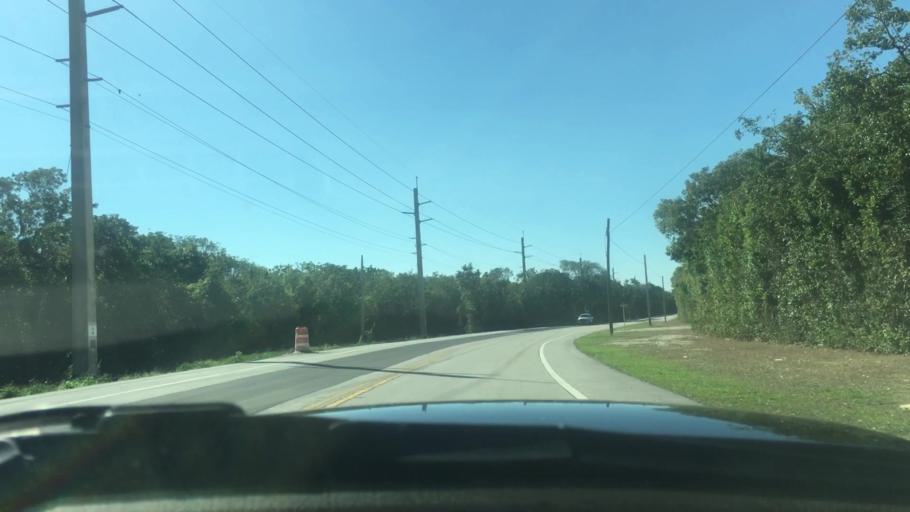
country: US
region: Florida
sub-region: Monroe County
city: North Key Largo
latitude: 25.2280
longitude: -80.3289
